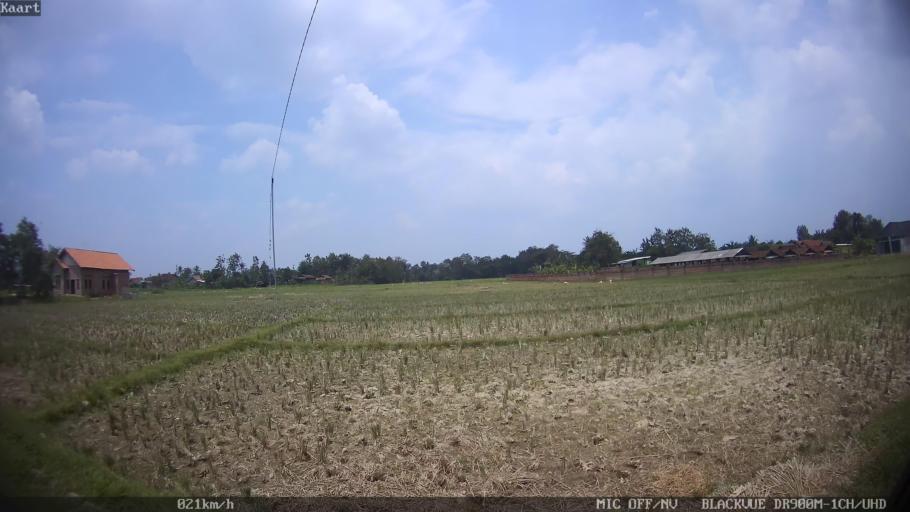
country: ID
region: Lampung
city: Gadingrejo
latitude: -5.3578
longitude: 105.0245
